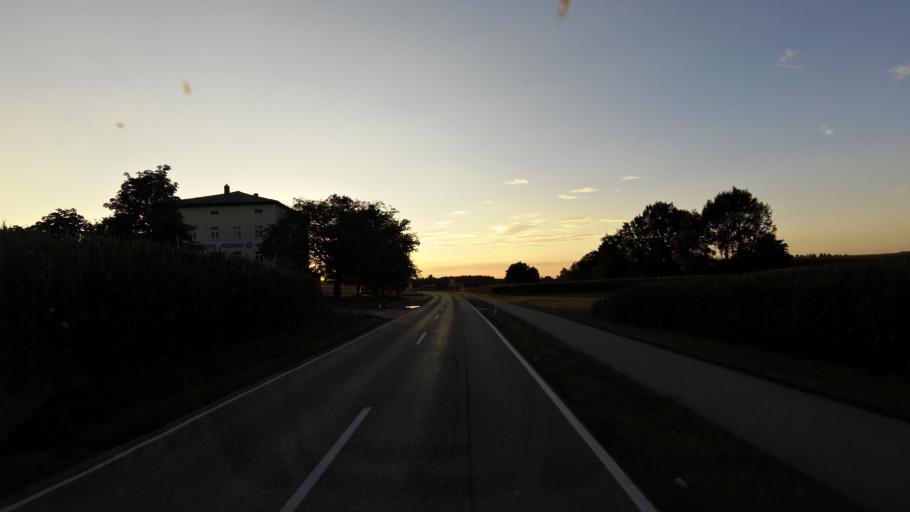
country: DE
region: Bavaria
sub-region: Upper Bavaria
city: Trostberg an der Alz
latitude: 48.0346
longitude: 12.5284
